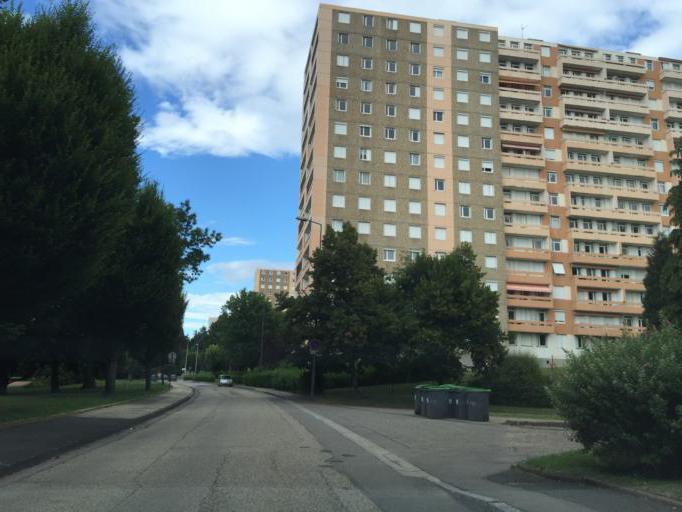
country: FR
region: Rhone-Alpes
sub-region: Departement de la Loire
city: Saint-Etienne
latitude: 45.4196
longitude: 4.4159
